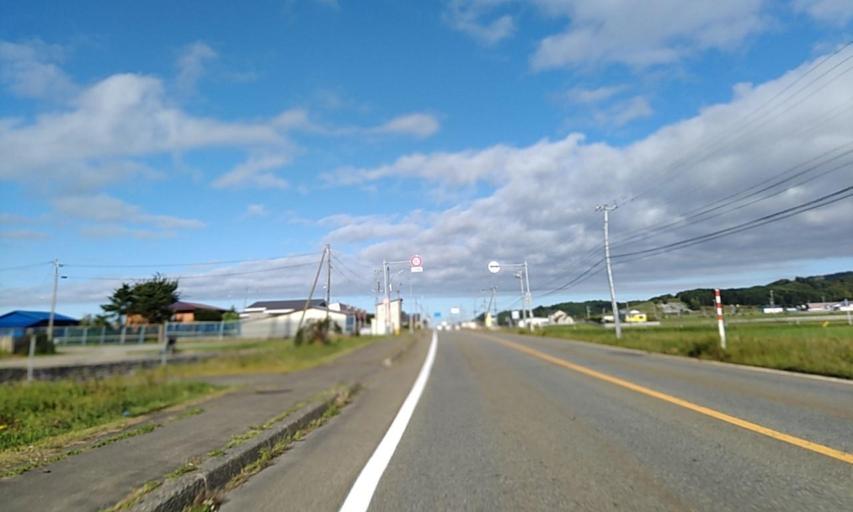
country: JP
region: Hokkaido
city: Shizunai-furukawacho
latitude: 42.2233
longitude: 142.6305
